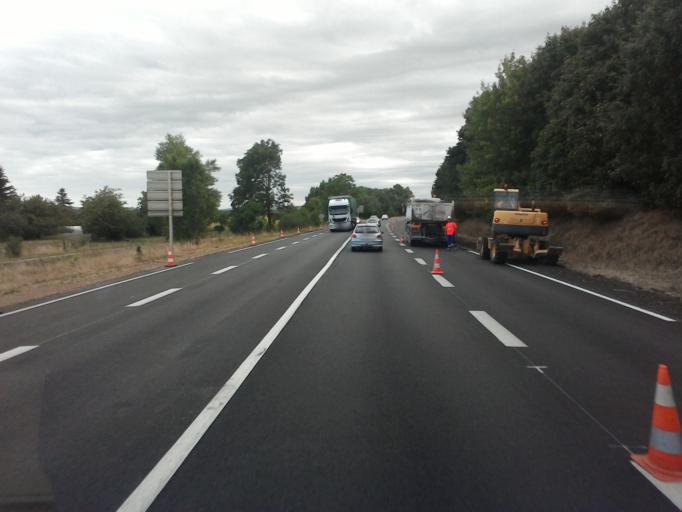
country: FR
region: Rhone-Alpes
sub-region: Departement de l'Ain
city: Saint-Denis-en-Bugey
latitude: 45.9586
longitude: 5.3280
